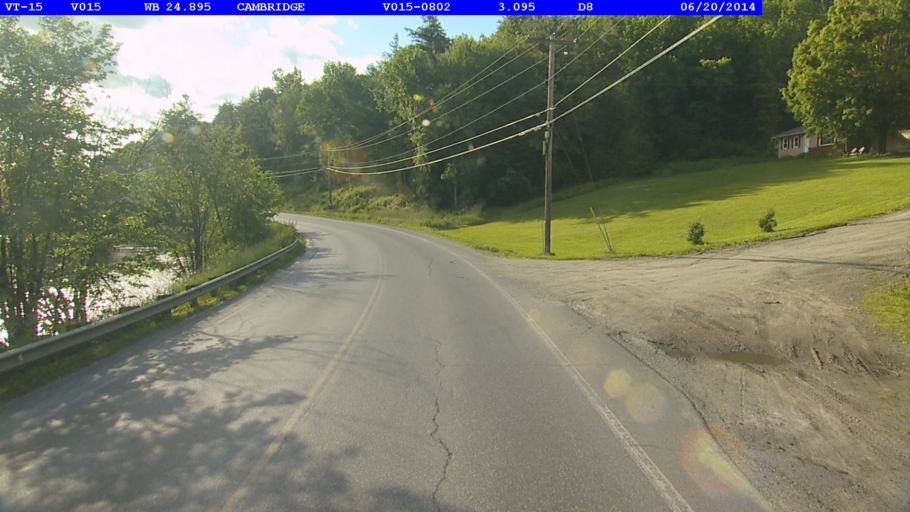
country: US
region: Vermont
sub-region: Lamoille County
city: Johnson
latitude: 44.6475
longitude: -72.8669
